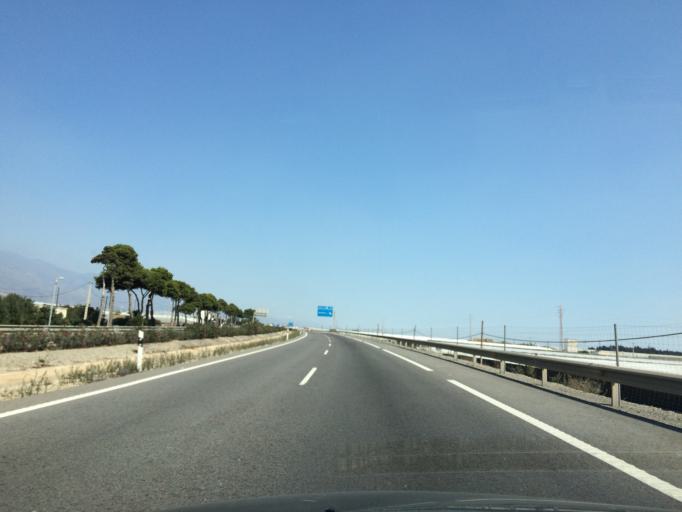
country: ES
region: Andalusia
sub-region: Provincia de Almeria
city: Dalias
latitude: 36.7553
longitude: -2.8807
